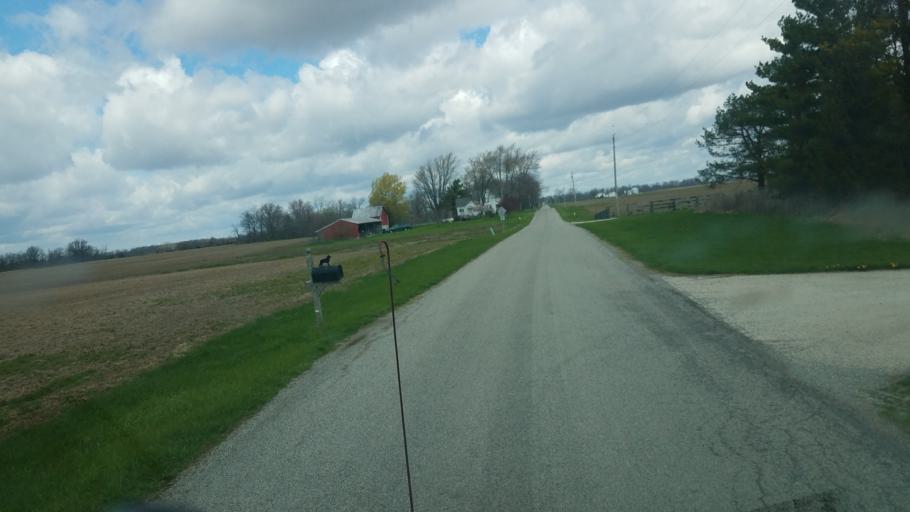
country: US
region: Ohio
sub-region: Union County
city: Richwood
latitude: 40.3754
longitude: -83.2575
